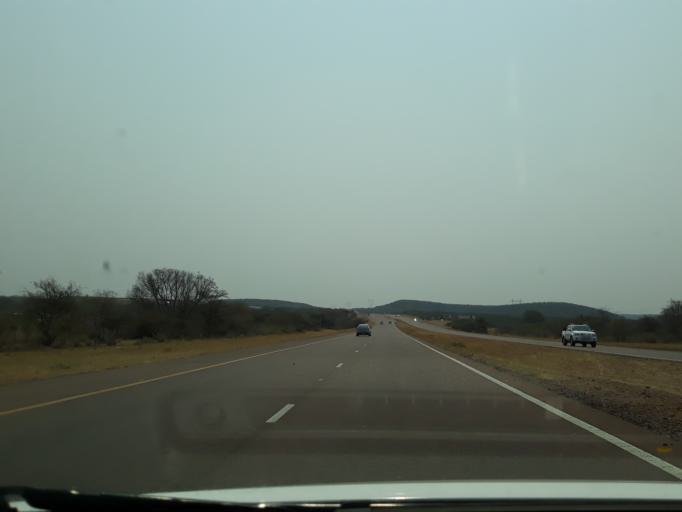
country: BW
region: Kgatleng
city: Bokaa
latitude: -24.4073
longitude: 26.0534
